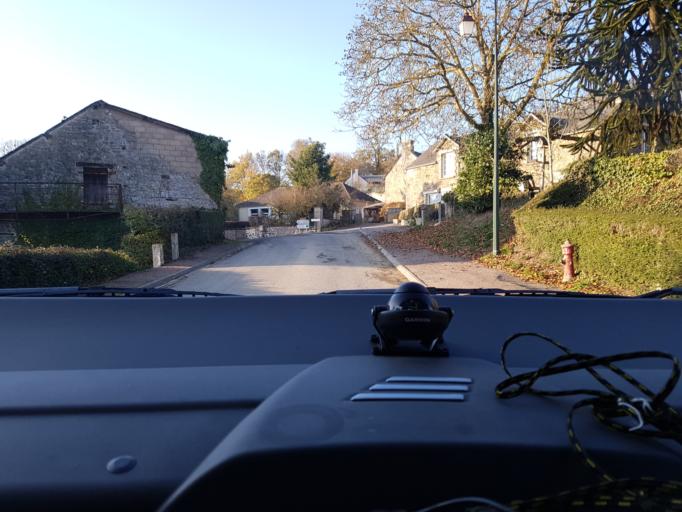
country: FR
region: Lower Normandy
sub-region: Departement du Calvados
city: Clecy
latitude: 48.9091
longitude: -0.4247
